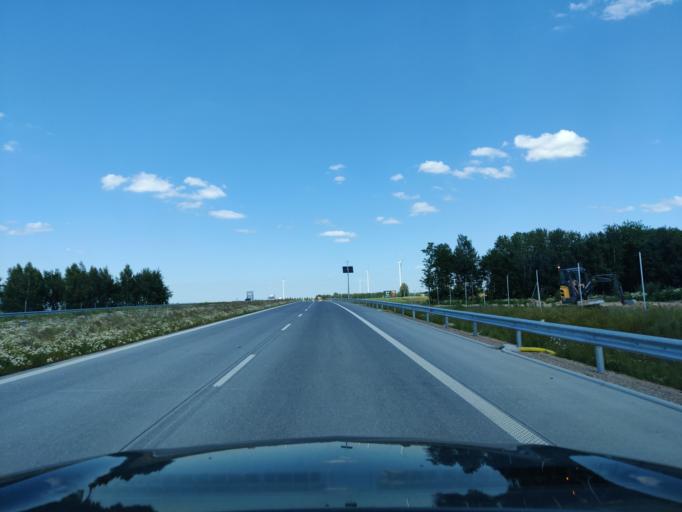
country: PL
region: Masovian Voivodeship
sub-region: Powiat mlawski
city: Wisniewo
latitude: 53.0338
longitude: 20.3528
